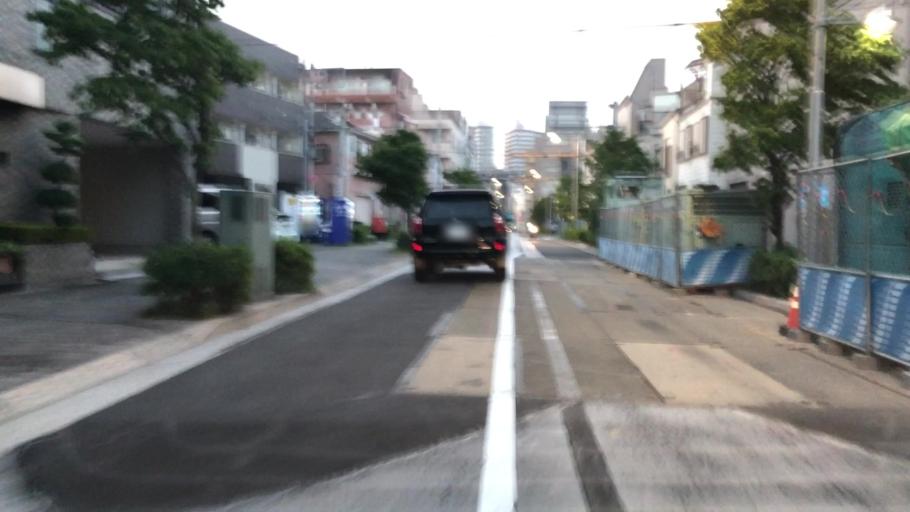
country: JP
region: Saitama
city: Soka
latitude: 35.7453
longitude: 139.7758
